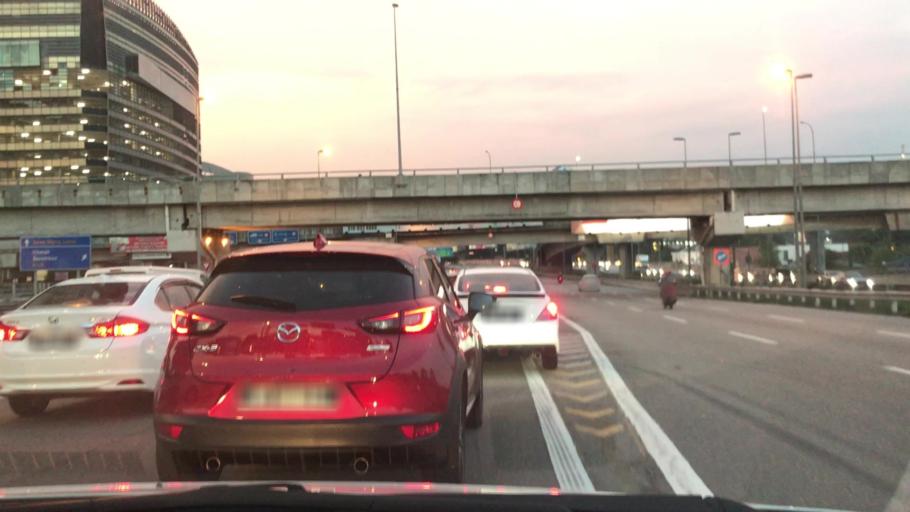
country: MY
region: Kuala Lumpur
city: Kuala Lumpur
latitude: 3.1149
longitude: 101.6742
